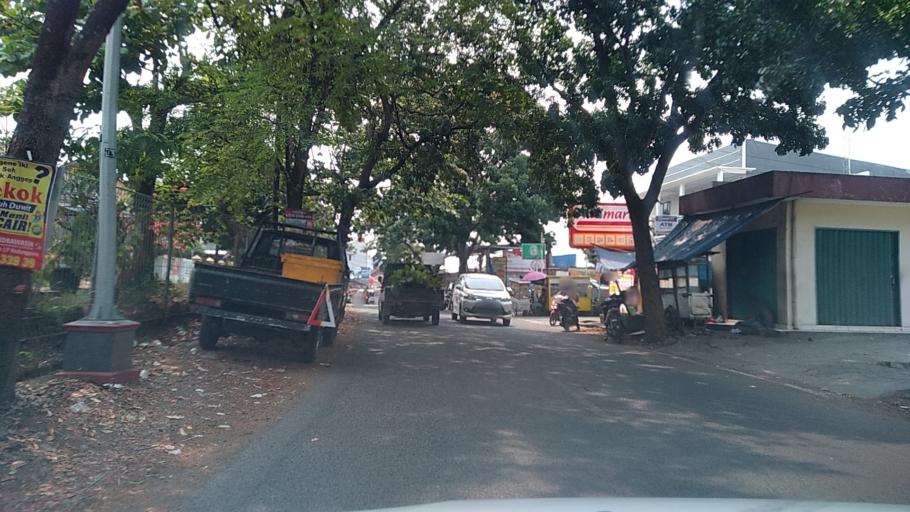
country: ID
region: Central Java
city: Semarang
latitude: -6.9966
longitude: 110.3356
